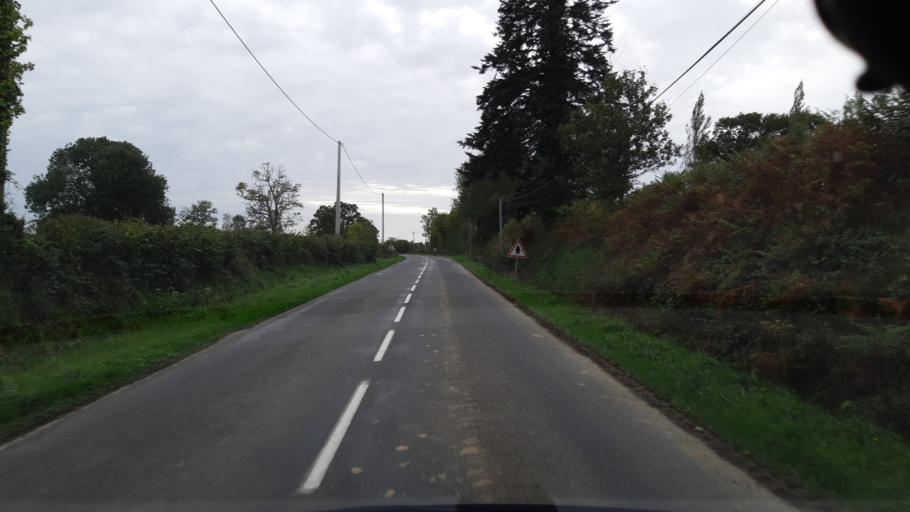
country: FR
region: Lower Normandy
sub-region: Departement de la Manche
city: Hambye
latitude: 48.9600
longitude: -1.2639
